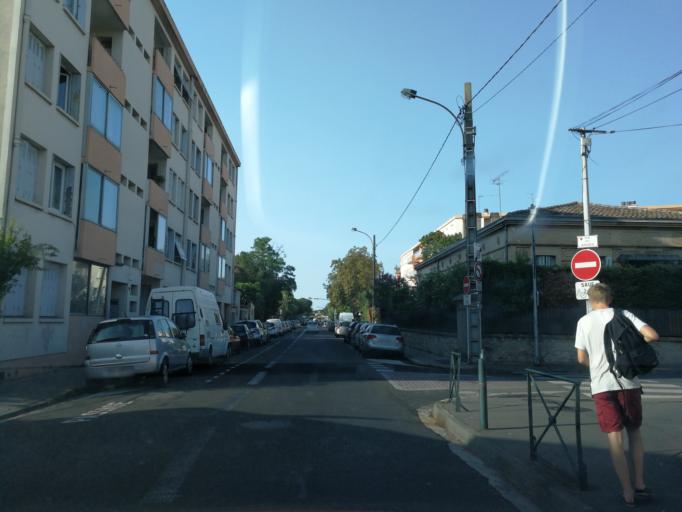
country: FR
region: Midi-Pyrenees
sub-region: Departement de la Haute-Garonne
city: Toulouse
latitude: 43.6213
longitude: 1.4371
